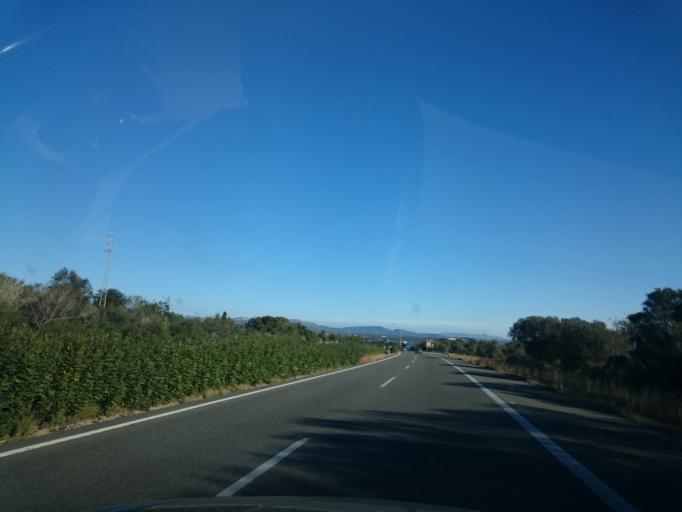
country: ES
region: Catalonia
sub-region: Provincia de Tarragona
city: Masdenverge
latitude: 40.7081
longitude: 0.5522
